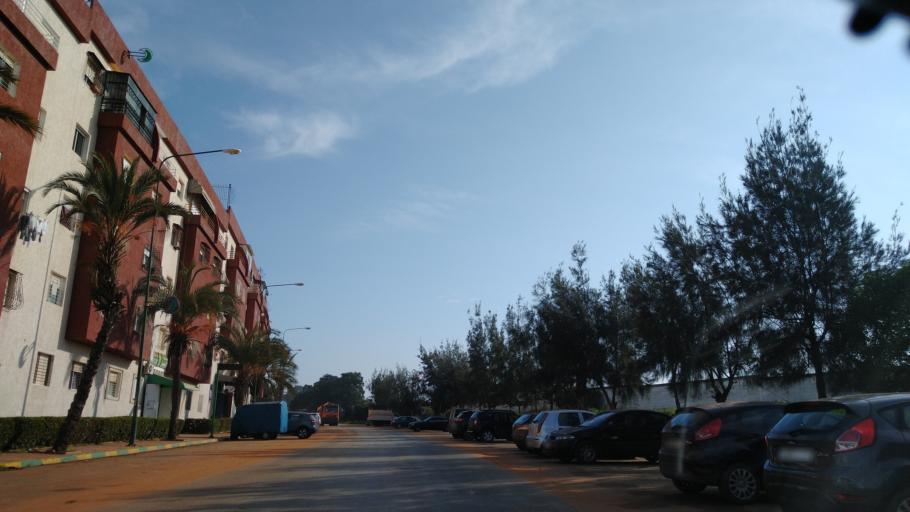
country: MA
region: Rabat-Sale-Zemmour-Zaer
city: Sale
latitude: 33.9868
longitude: -6.7382
